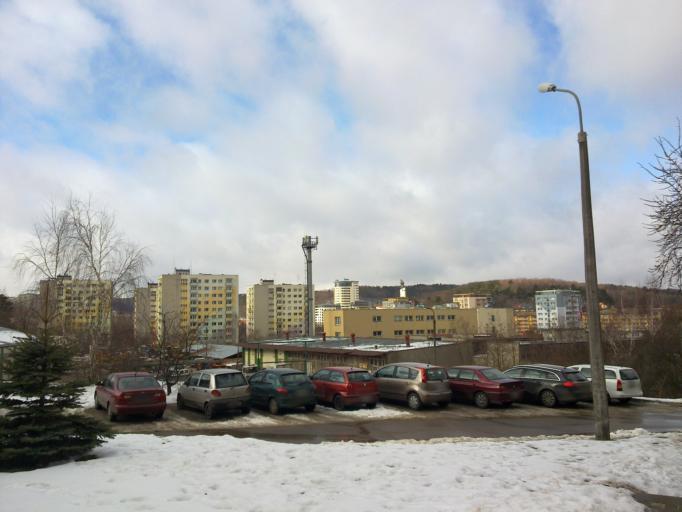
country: PL
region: Pomeranian Voivodeship
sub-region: Gdansk
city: Gdansk
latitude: 54.3772
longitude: 18.5880
